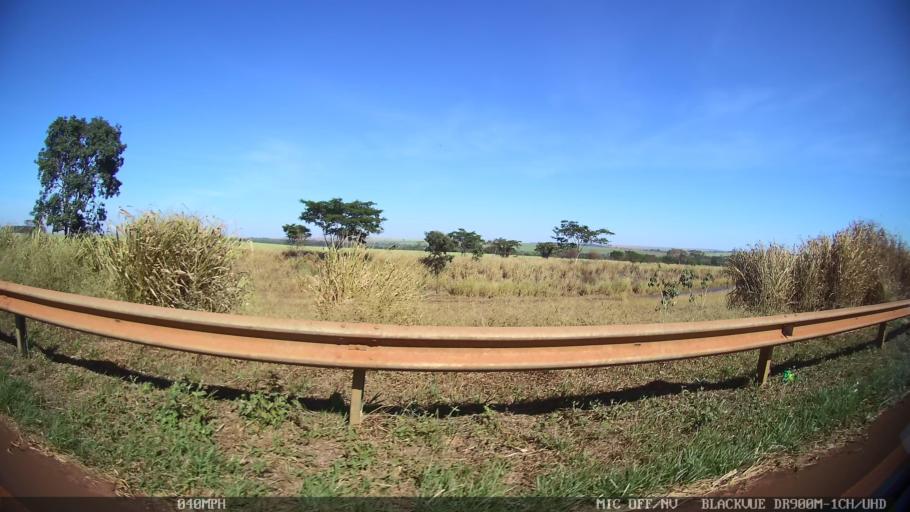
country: BR
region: Sao Paulo
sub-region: Barretos
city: Barretos
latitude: -20.4467
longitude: -48.4494
